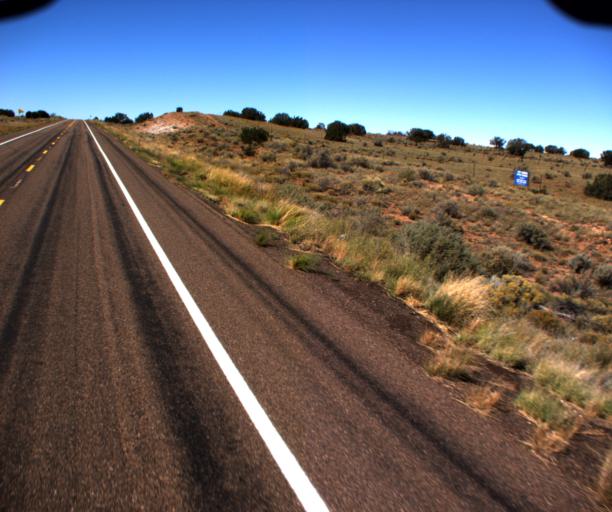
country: US
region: Arizona
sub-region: Apache County
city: Saint Johns
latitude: 34.5940
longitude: -109.6174
